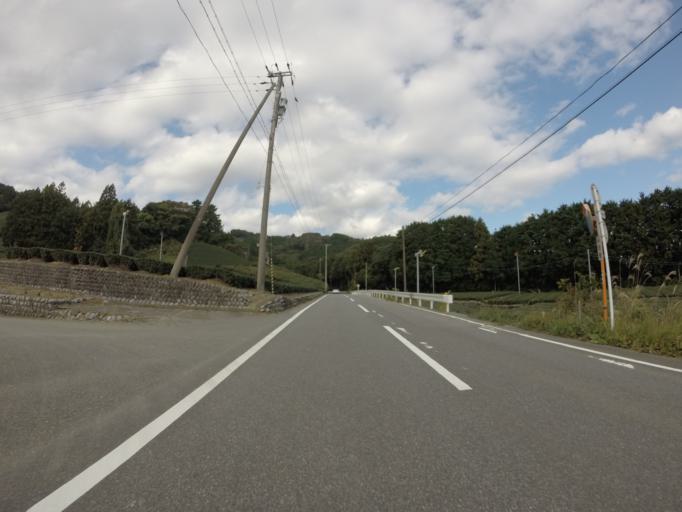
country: JP
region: Shizuoka
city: Kanaya
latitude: 34.8635
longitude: 138.1050
